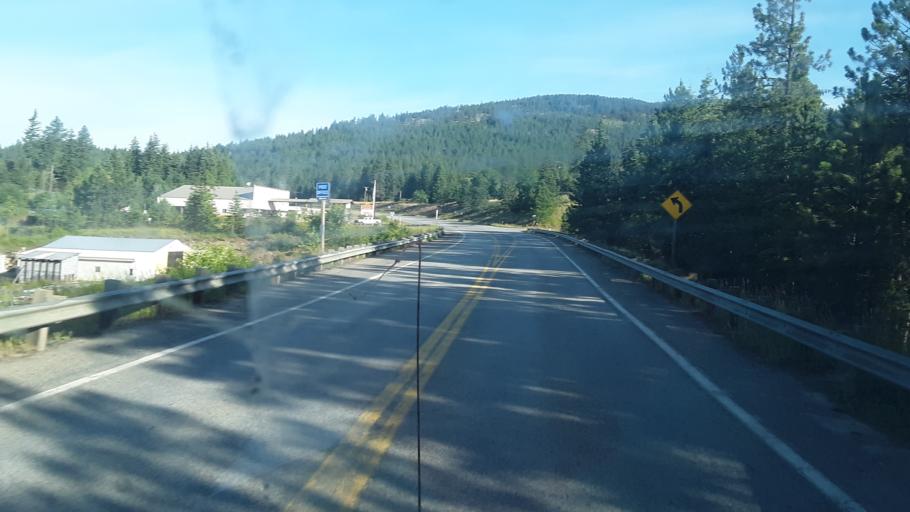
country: US
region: Idaho
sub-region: Boundary County
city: Bonners Ferry
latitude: 48.7307
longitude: -116.1809
